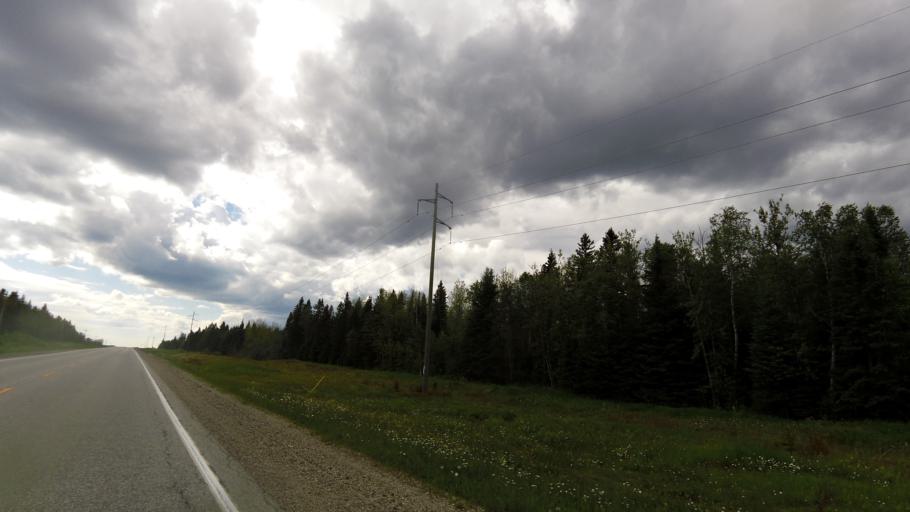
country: CA
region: Ontario
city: Hearst
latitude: 49.7457
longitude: -84.1501
